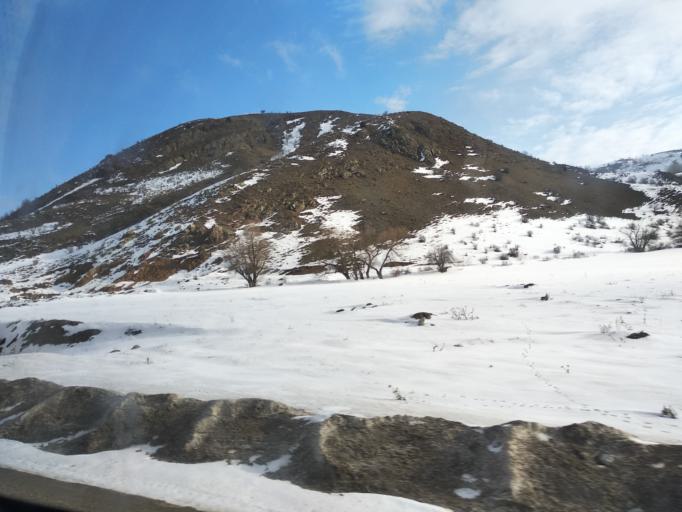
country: TR
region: Erzincan
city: Catalarmut
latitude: 39.9115
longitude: 39.4096
